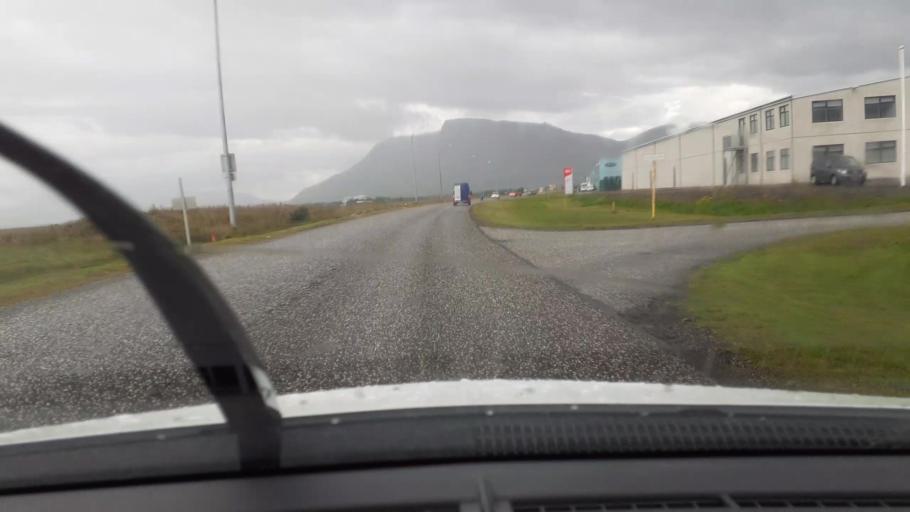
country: IS
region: West
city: Akranes
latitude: 64.3270
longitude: -22.0621
